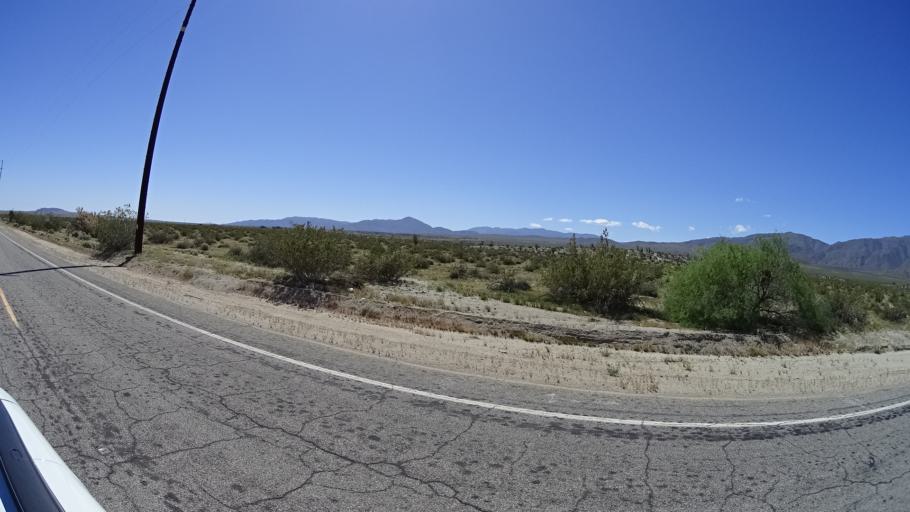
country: US
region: California
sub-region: San Diego County
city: Borrego Springs
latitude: 33.2208
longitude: -116.3401
